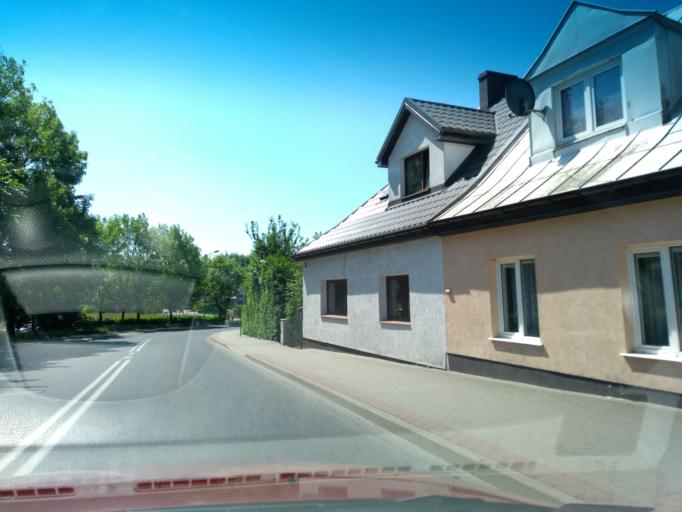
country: PL
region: West Pomeranian Voivodeship
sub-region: Koszalin
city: Koszalin
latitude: 54.2054
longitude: 16.1759
